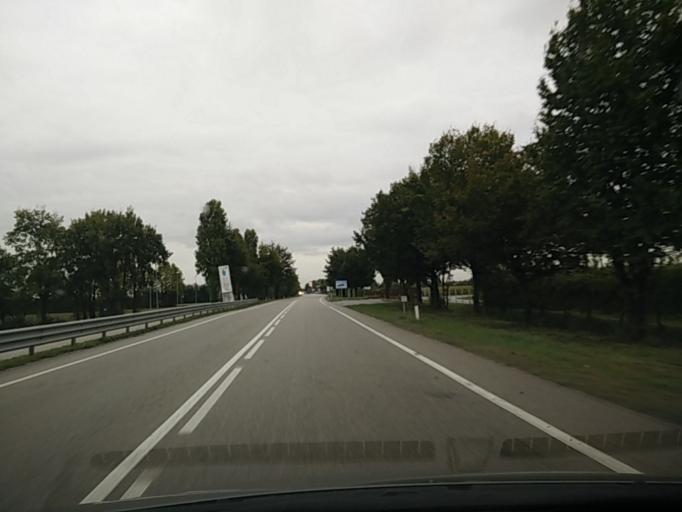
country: IT
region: Veneto
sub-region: Provincia di Treviso
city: Roncade
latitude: 45.6388
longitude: 12.3907
